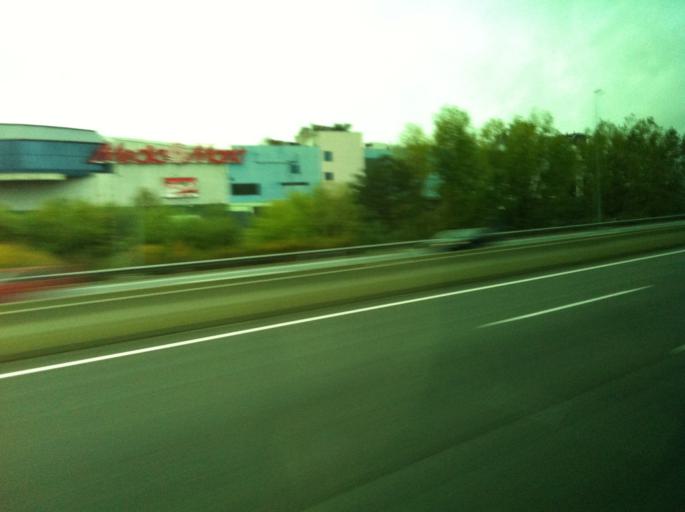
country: ES
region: Madrid
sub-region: Provincia de Madrid
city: Collado-Villalba
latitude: 40.6375
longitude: -4.0153
